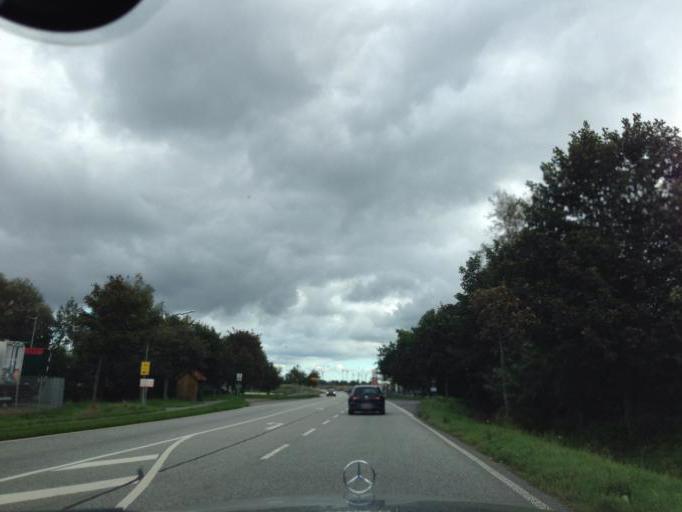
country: DE
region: Schleswig-Holstein
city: Stadum
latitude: 54.7424
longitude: 9.0519
